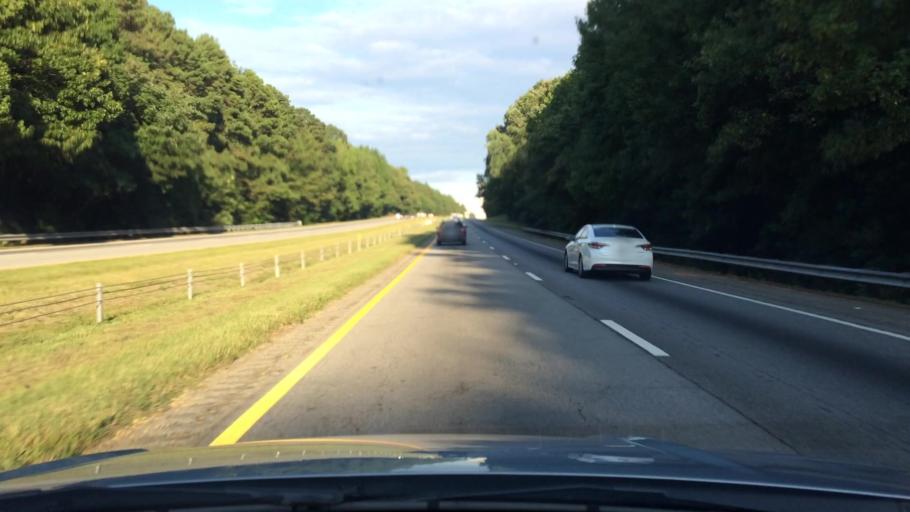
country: US
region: South Carolina
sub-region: Lexington County
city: Chapin
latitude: 34.2073
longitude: -81.3777
